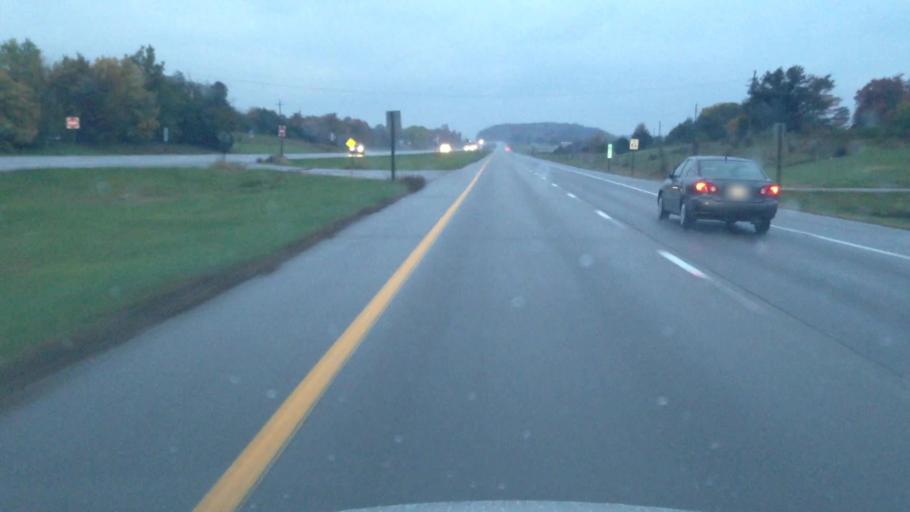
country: US
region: Kansas
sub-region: Douglas County
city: Lawrence
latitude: 38.9070
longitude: -95.2607
